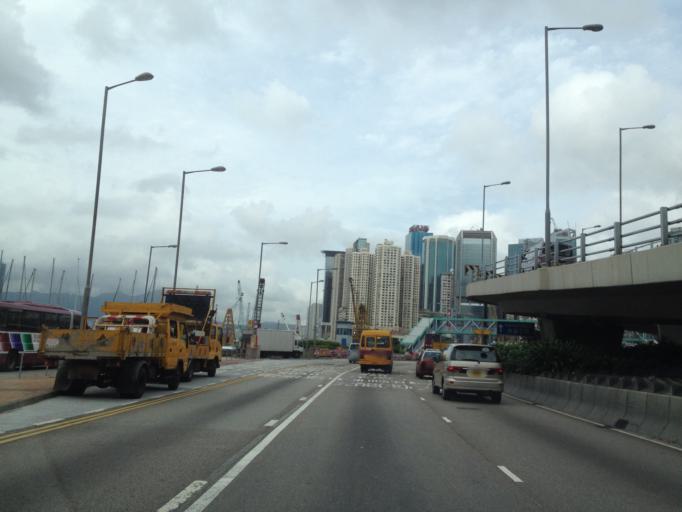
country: HK
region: Wanchai
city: Wan Chai
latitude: 22.2834
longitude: 114.1851
